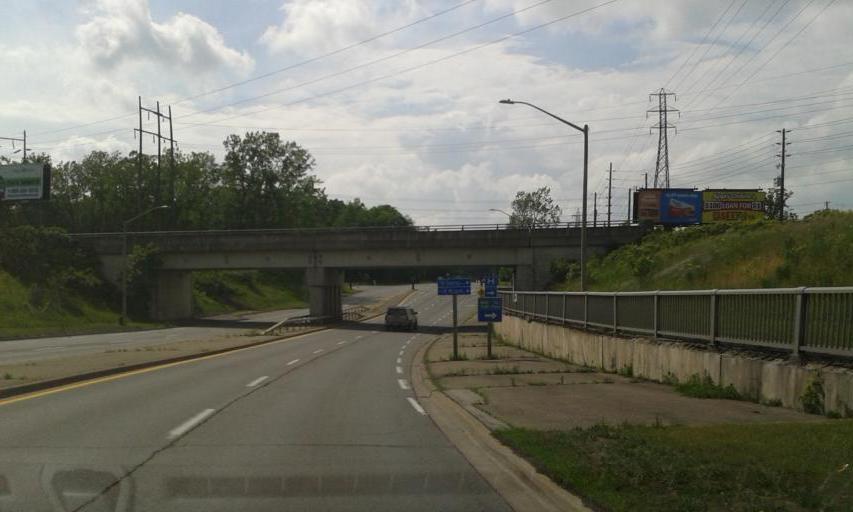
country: CA
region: Ontario
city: Niagara Falls
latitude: 43.0684
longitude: -79.0822
